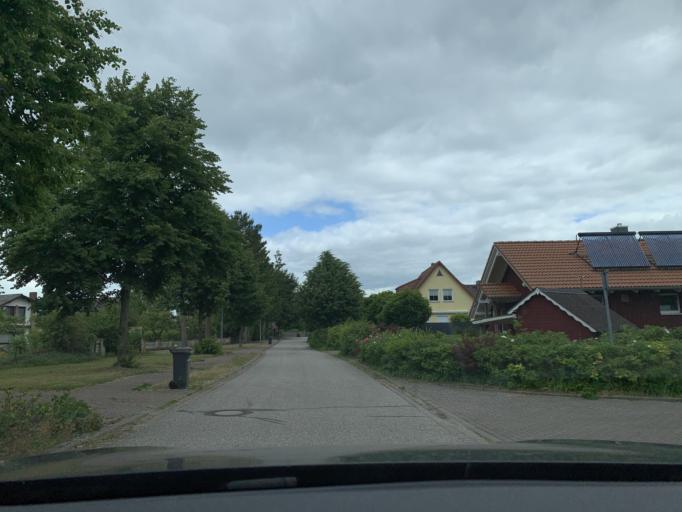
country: DE
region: Mecklenburg-Vorpommern
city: Rechlin
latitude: 53.3539
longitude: 12.7216
